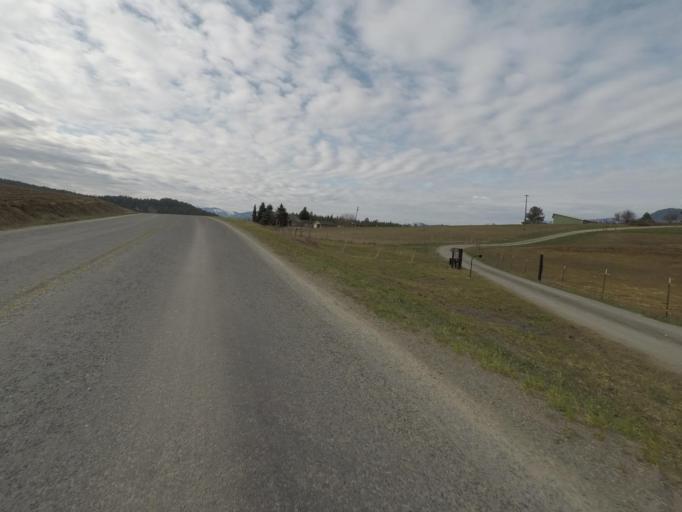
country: US
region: Washington
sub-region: Stevens County
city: Colville
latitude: 48.5242
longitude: -117.8814
